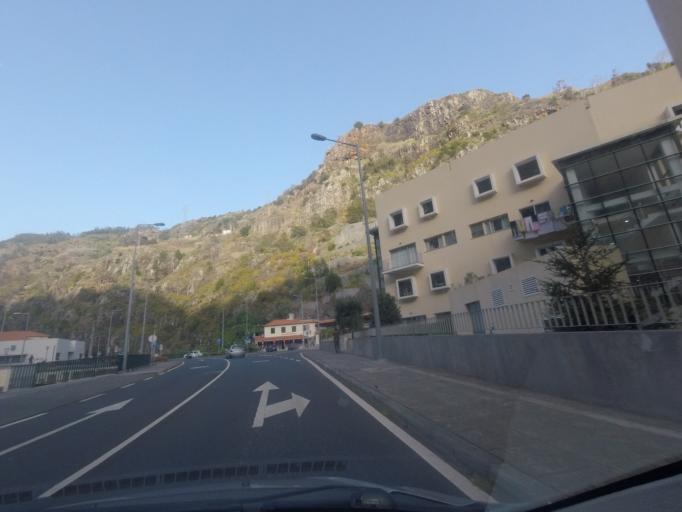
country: PT
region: Madeira
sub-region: Ribeira Brava
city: Campanario
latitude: 32.6794
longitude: -17.0583
